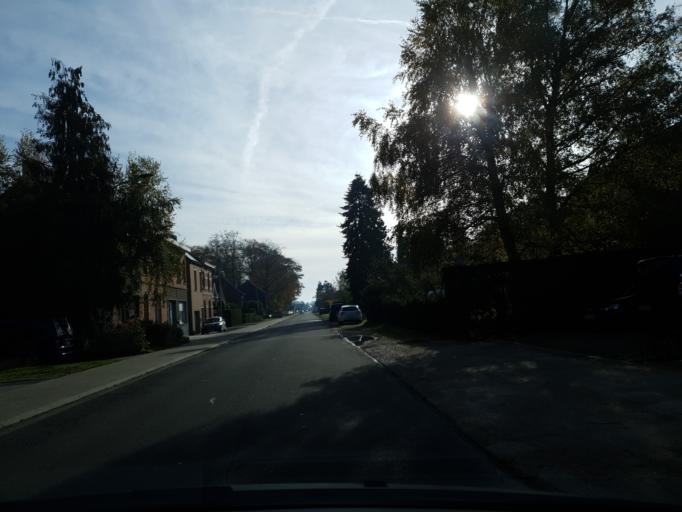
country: BE
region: Flanders
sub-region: Provincie Oost-Vlaanderen
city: Sint-Niklaas
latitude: 51.1504
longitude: 4.1728
